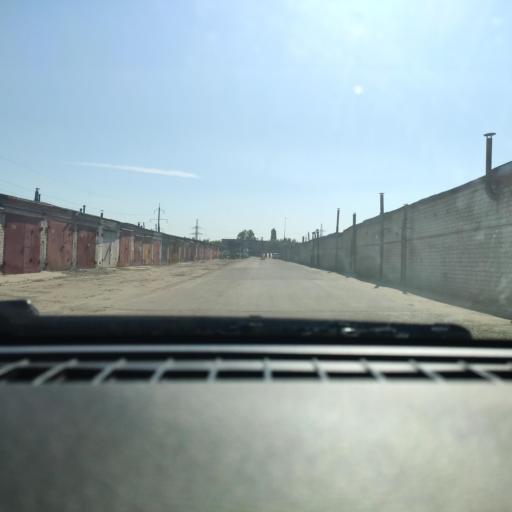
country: RU
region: Voronezj
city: Maslovka
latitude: 51.6170
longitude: 39.2633
